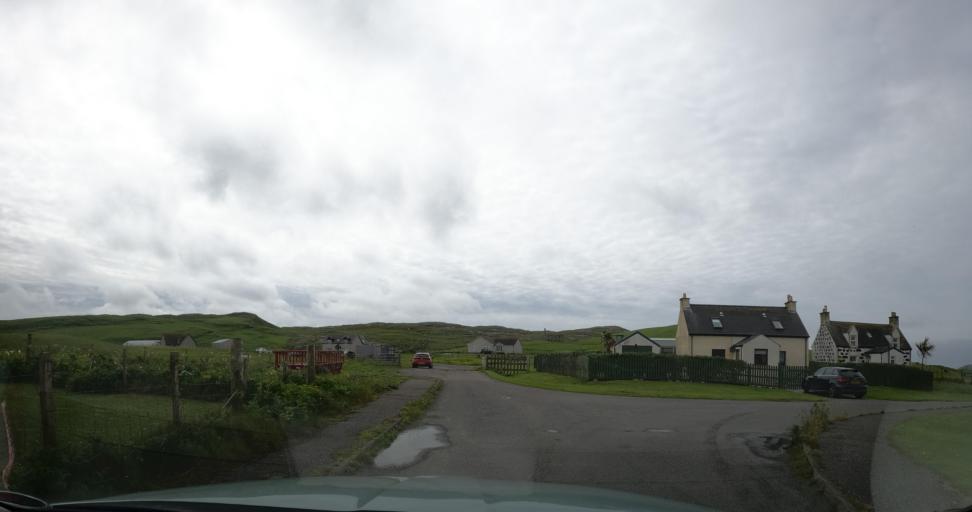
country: GB
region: Scotland
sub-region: Eilean Siar
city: Barra
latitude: 56.9189
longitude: -7.5371
